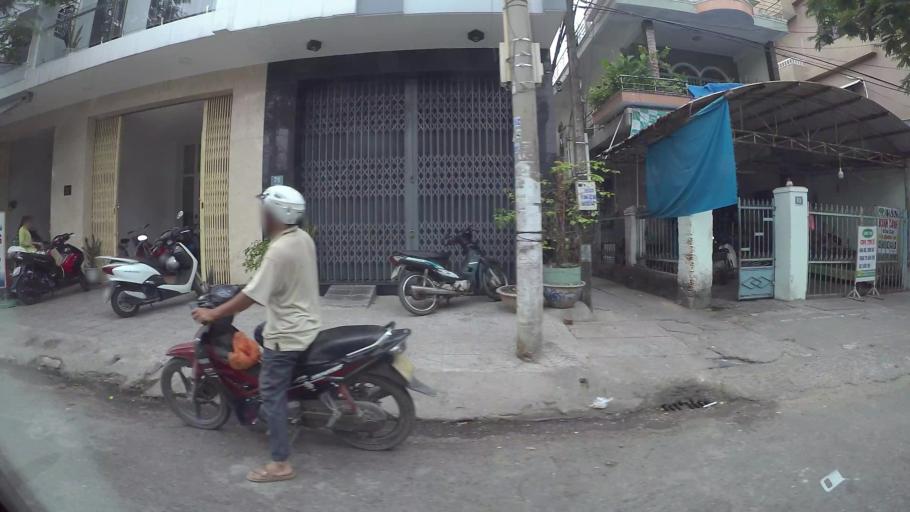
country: VN
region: Da Nang
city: Thanh Khe
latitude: 16.0737
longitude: 108.1772
